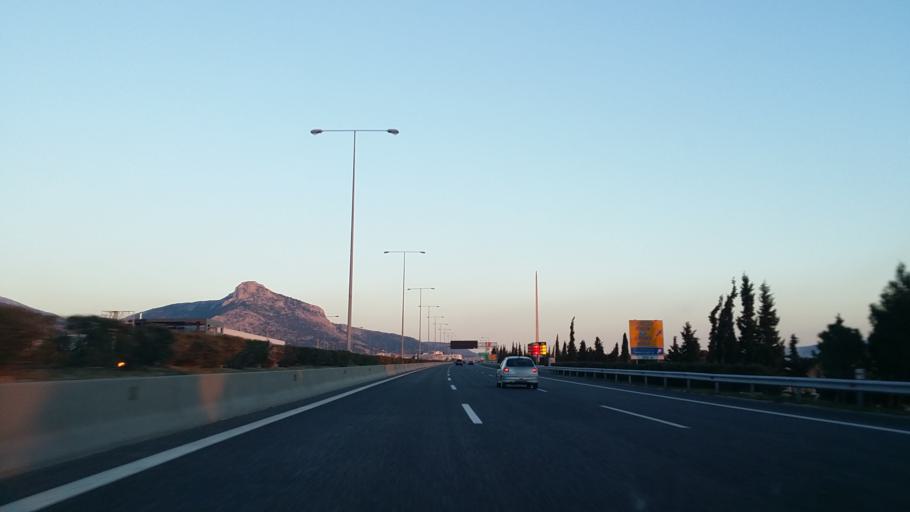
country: GR
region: Attica
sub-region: Nomarchia Dytikis Attikis
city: Aspropyrgos
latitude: 38.0940
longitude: 23.5957
